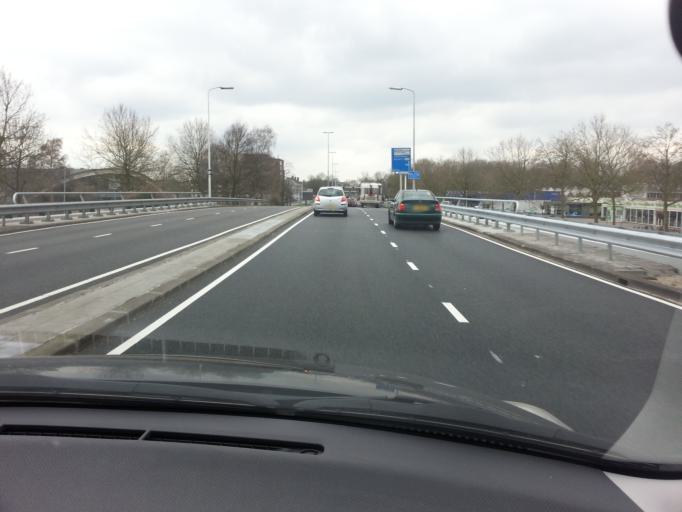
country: NL
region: North Brabant
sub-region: Gemeente Eindhoven
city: Lakerlopen
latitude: 51.4337
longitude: 5.5035
